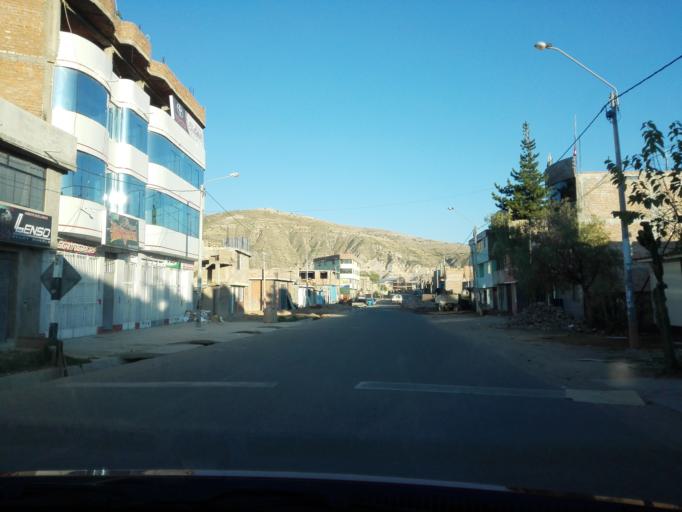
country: PE
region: Ayacucho
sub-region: Provincia de Huamanga
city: Ayacucho
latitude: -13.1361
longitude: -74.2257
